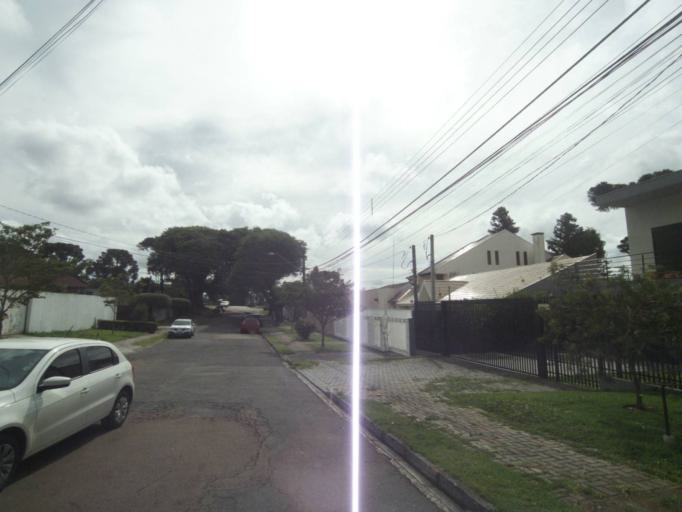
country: BR
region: Parana
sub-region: Curitiba
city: Curitiba
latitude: -25.4391
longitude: -49.2988
